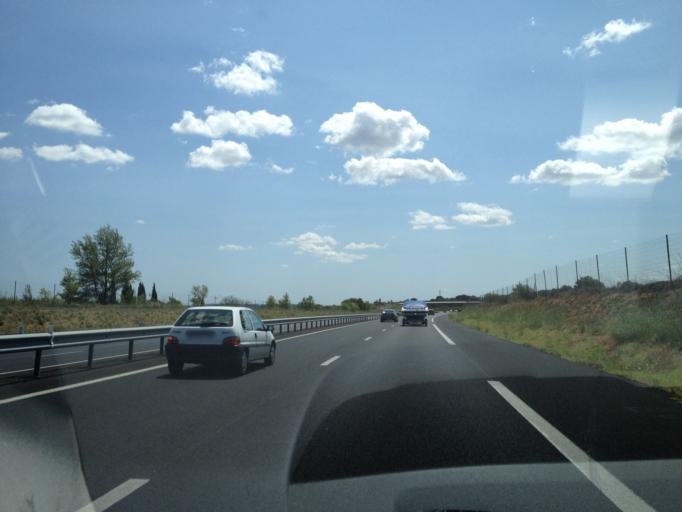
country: FR
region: Languedoc-Roussillon
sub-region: Departement de l'Herault
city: Aspiran
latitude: 43.5817
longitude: 3.4658
